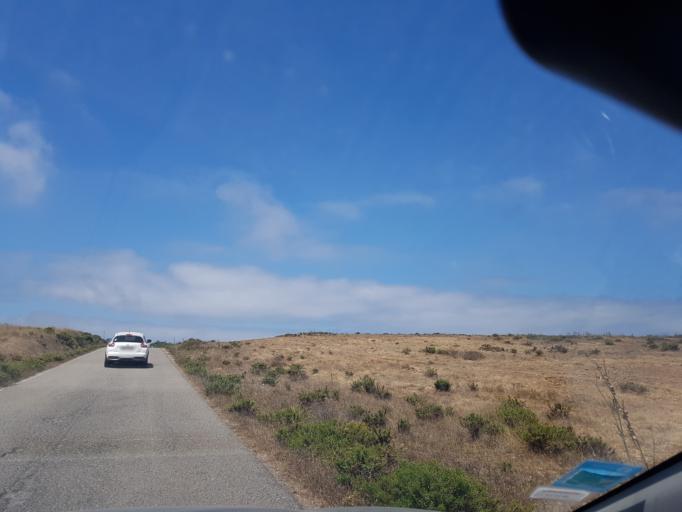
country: PT
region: Faro
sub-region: Vila do Bispo
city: Vila do Bispo
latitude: 37.0904
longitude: -8.9267
